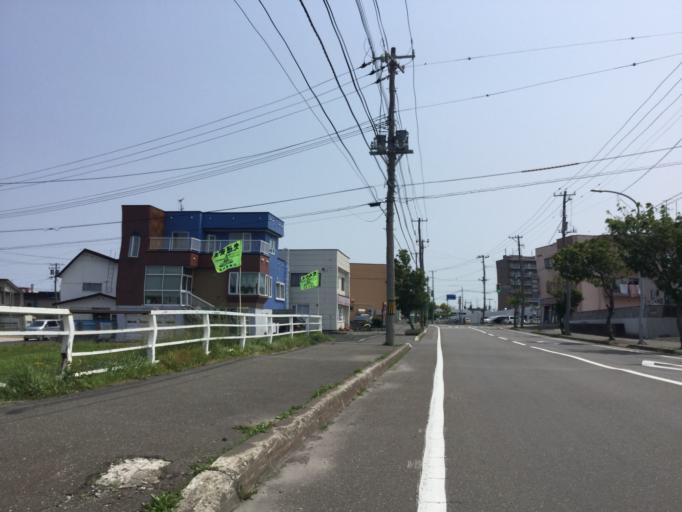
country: JP
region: Hokkaido
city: Wakkanai
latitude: 45.3953
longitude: 141.6958
